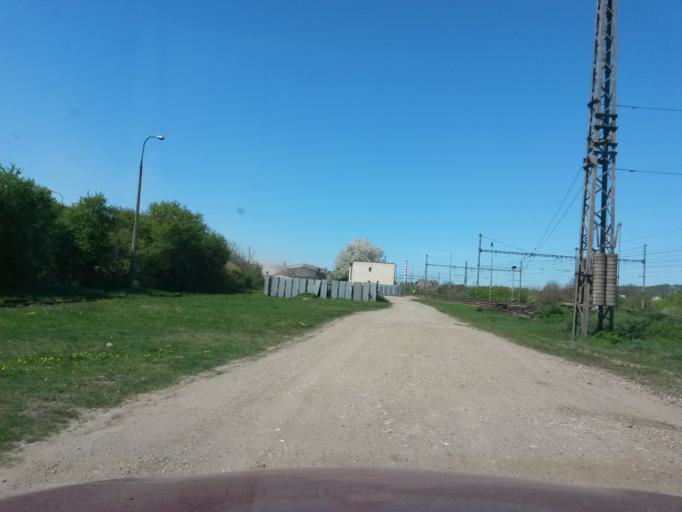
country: SK
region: Kosicky
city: Kosice
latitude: 48.6813
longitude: 21.2752
